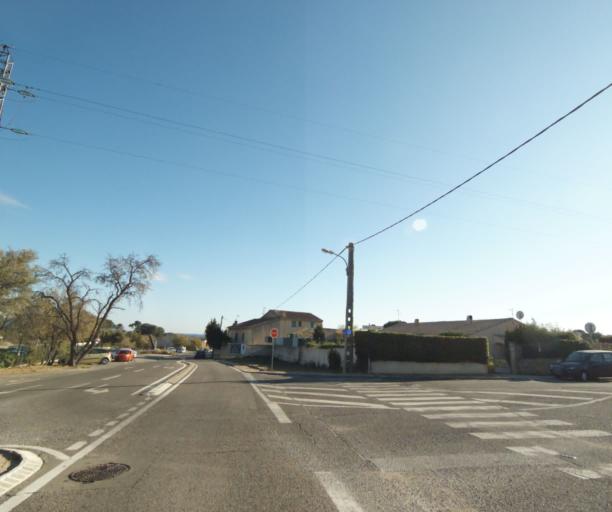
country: FR
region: Provence-Alpes-Cote d'Azur
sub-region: Departement des Bouches-du-Rhone
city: La Ciotat
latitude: 43.1925
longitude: 5.6012
